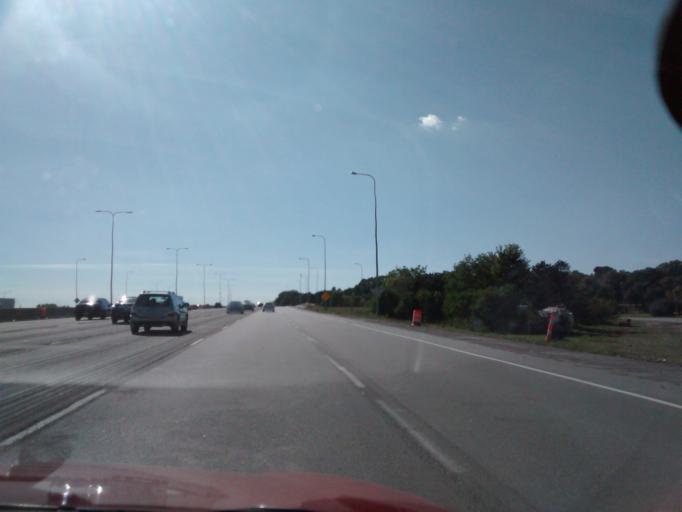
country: US
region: Nebraska
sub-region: Douglas County
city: Omaha
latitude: 41.2255
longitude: -95.9720
